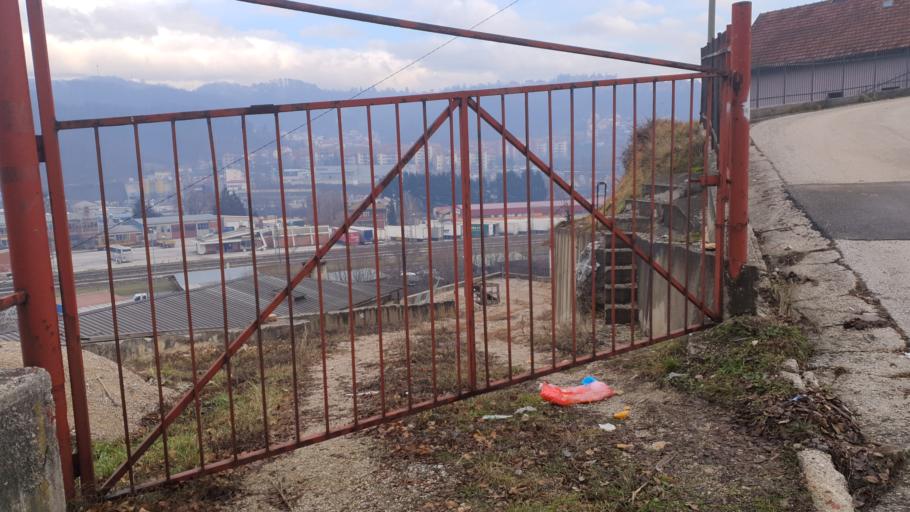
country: RS
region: Central Serbia
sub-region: Zlatiborski Okrug
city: Uzice
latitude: 43.8461
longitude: 19.8565
